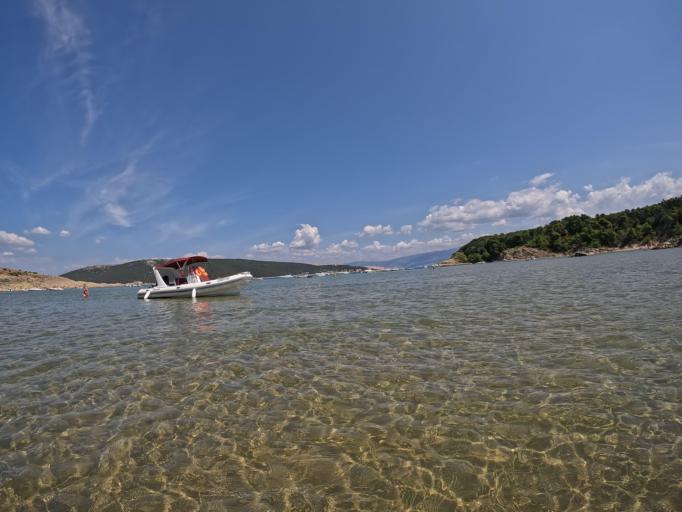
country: HR
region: Primorsko-Goranska
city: Lopar
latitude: 44.8404
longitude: 14.7525
